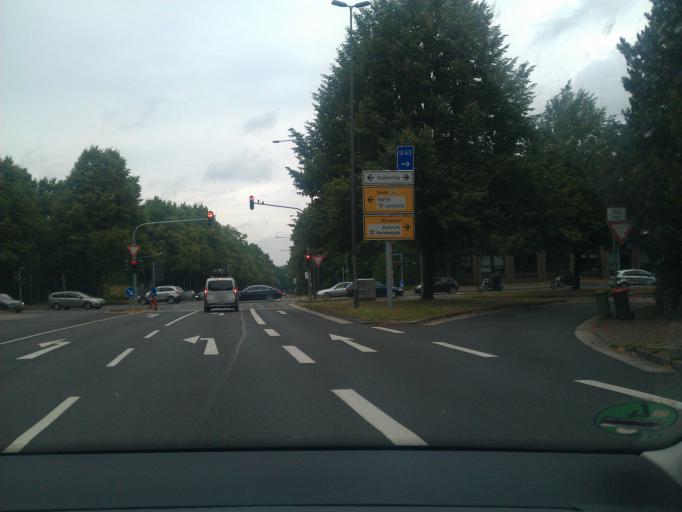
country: DE
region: North Rhine-Westphalia
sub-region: Regierungsbezirk Koln
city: Aachen
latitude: 50.7519
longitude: 6.0987
